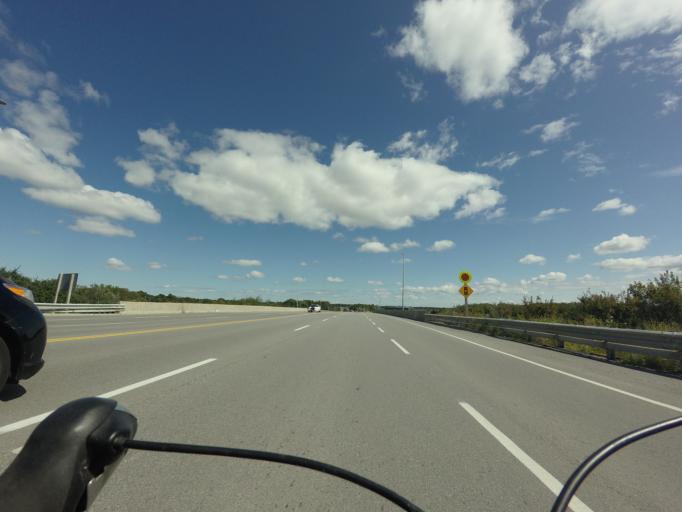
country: CA
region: Ontario
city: Bells Corners
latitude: 45.2707
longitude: -75.7967
